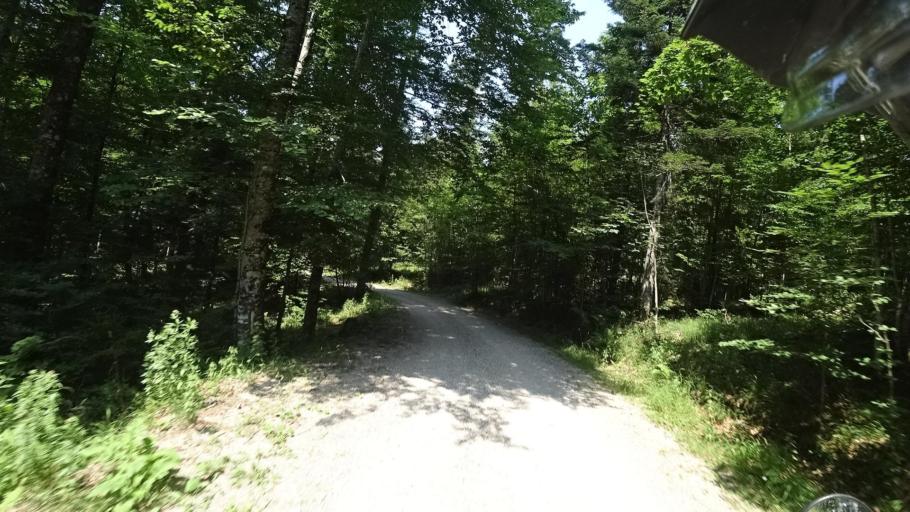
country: HR
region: Primorsko-Goranska
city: Vrbovsko
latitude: 45.2978
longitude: 15.1007
